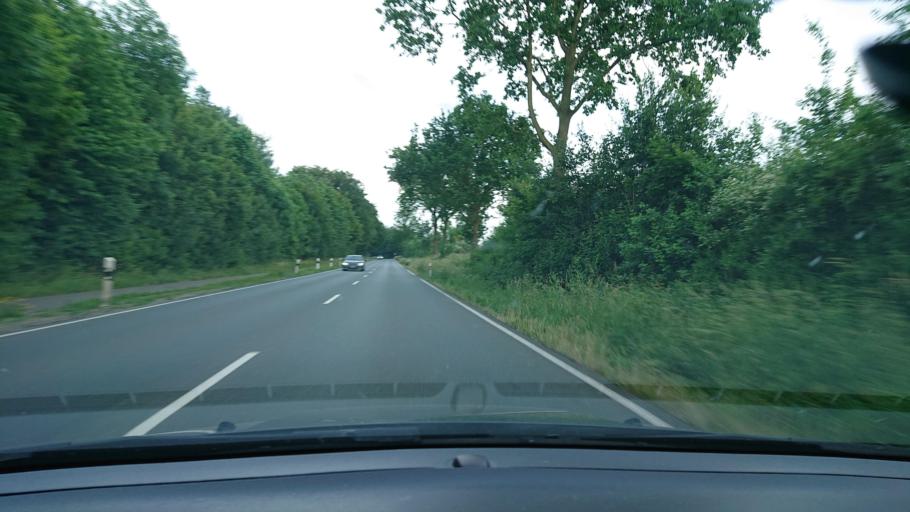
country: DE
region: North Rhine-Westphalia
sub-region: Regierungsbezirk Detmold
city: Hiddenhausen
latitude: 52.1730
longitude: 8.6211
